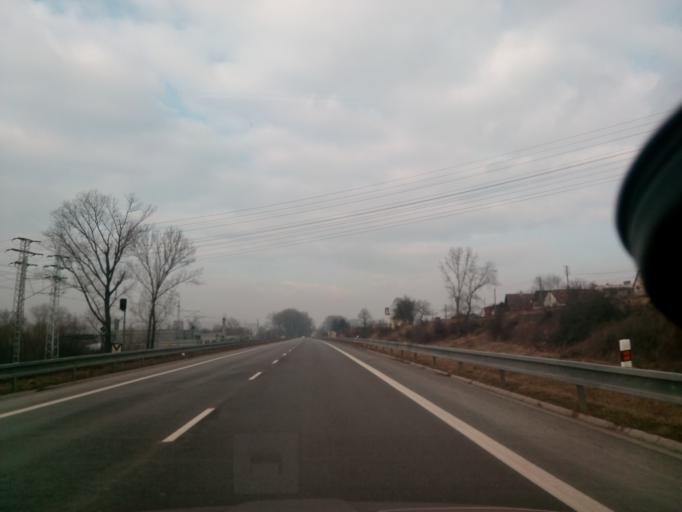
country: SK
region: Presovsky
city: Lipany
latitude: 49.1471
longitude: 20.9783
